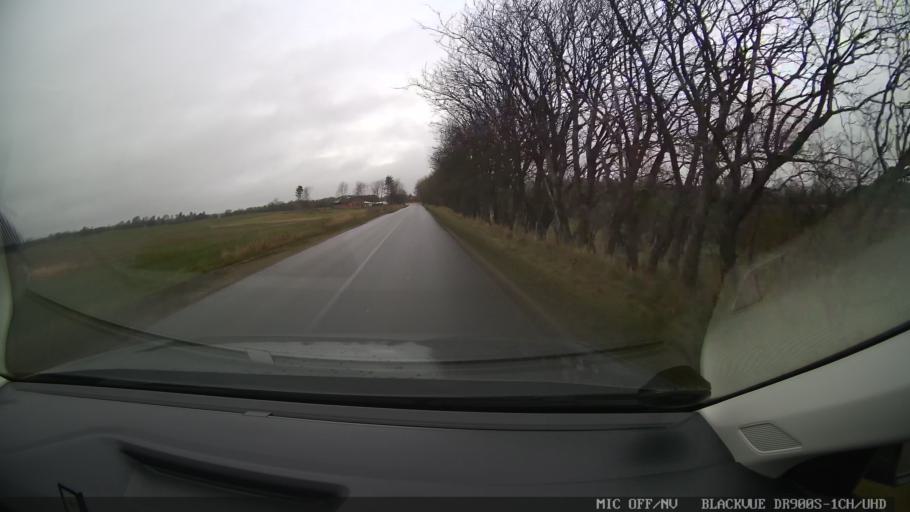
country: DK
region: Central Jutland
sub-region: Viborg Kommune
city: Karup
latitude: 56.3489
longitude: 9.2875
